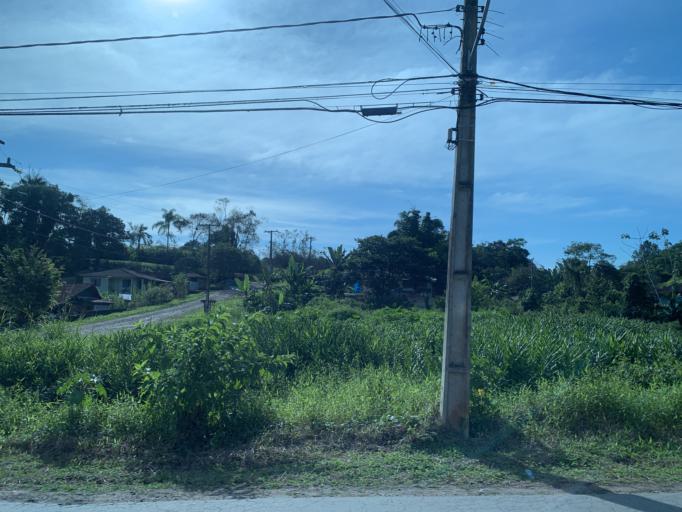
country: BR
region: Parana
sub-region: Antonina
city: Antonina
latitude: -25.4371
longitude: -48.7475
